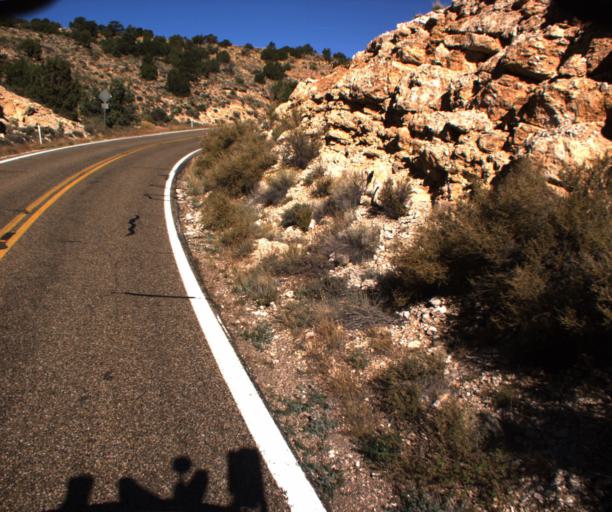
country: US
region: Arizona
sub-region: Coconino County
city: Fredonia
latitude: 36.7234
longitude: -112.0642
